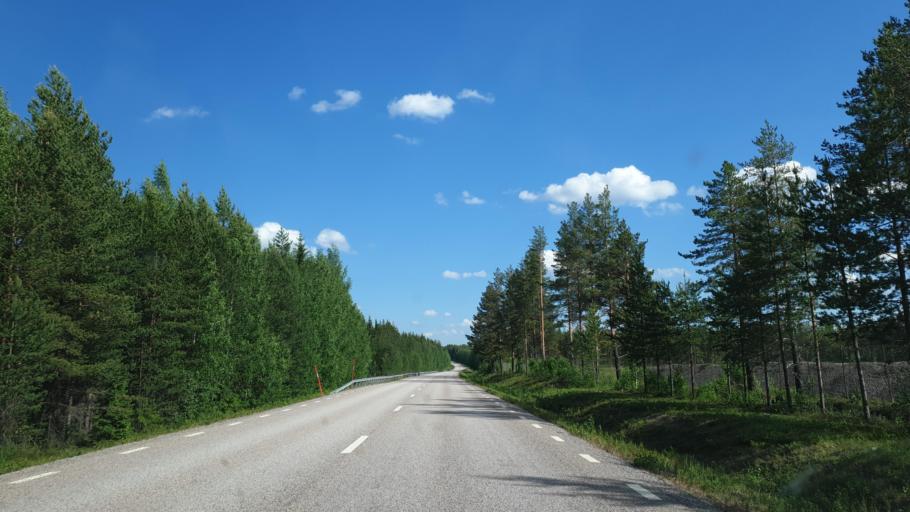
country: SE
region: Norrbotten
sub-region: Alvsbyns Kommun
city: AElvsbyn
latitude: 65.8086
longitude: 20.6049
